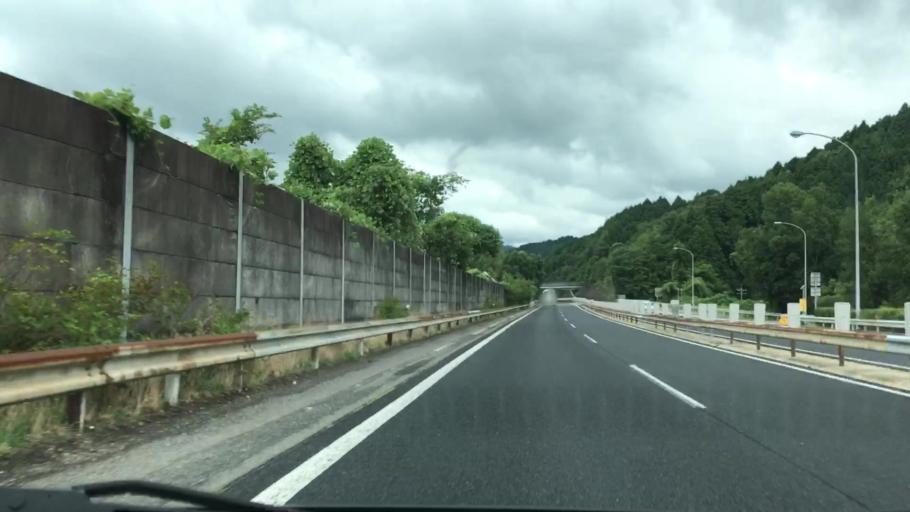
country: JP
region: Okayama
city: Takahashi
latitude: 35.0044
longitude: 133.7278
